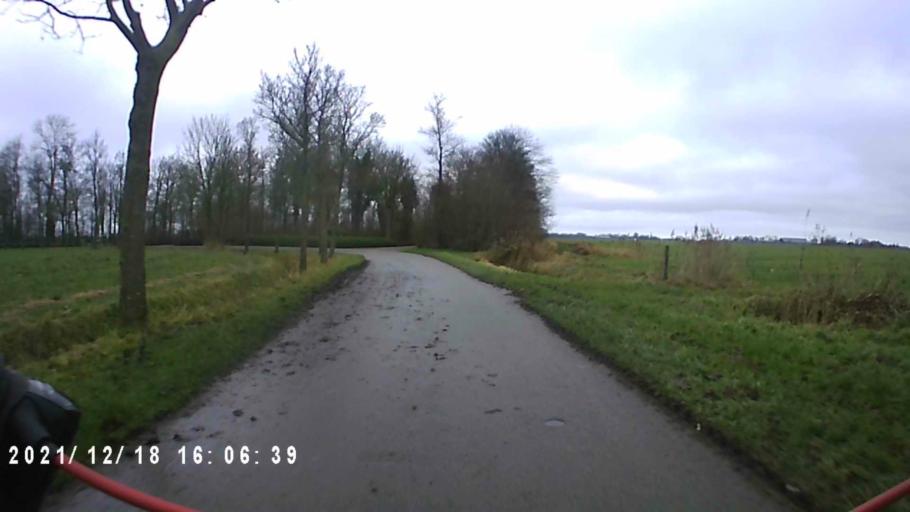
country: NL
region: Friesland
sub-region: Gemeente Dongeradeel
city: Anjum
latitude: 53.3570
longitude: 6.0777
